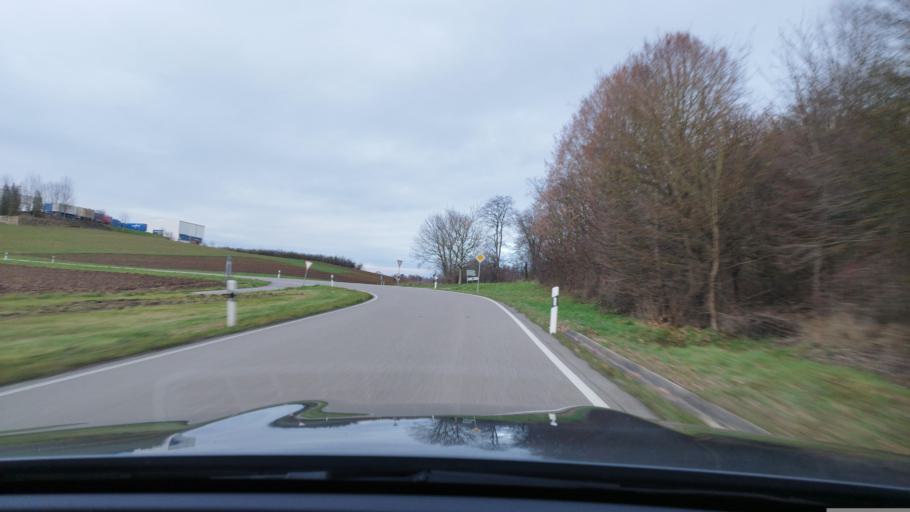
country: DE
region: Baden-Wuerttemberg
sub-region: Regierungsbezirk Stuttgart
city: Kirchberg an der Murr
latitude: 48.9407
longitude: 9.3582
